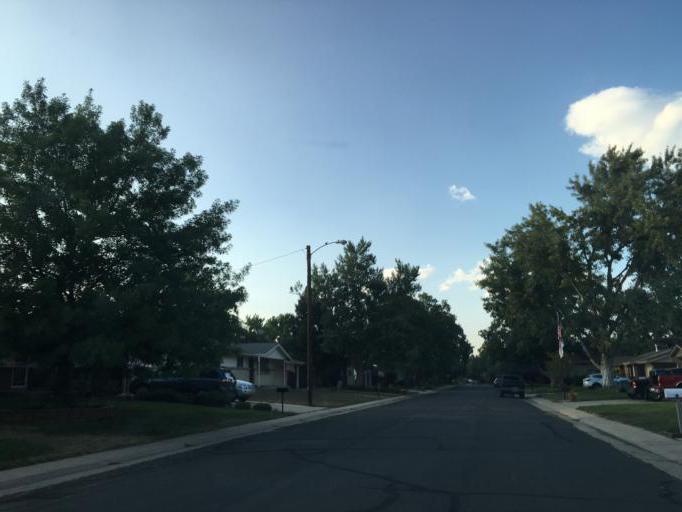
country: US
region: Colorado
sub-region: Jefferson County
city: Applewood
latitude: 39.7895
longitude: -105.1460
